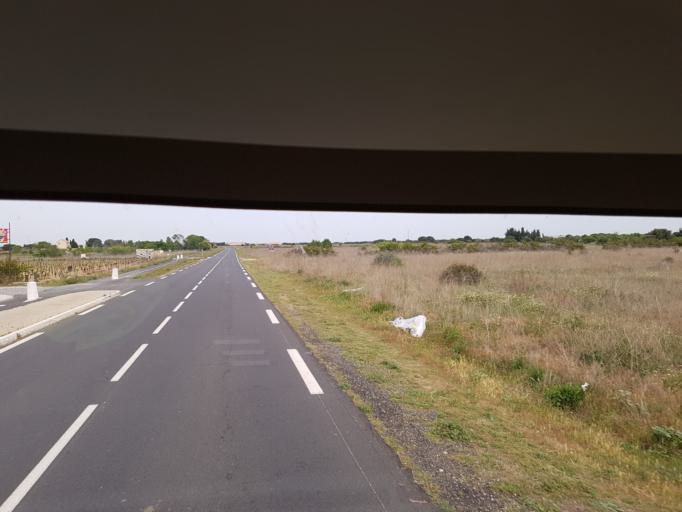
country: FR
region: Languedoc-Roussillon
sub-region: Departement de l'Herault
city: Vendres
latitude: 43.2707
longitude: 3.2477
